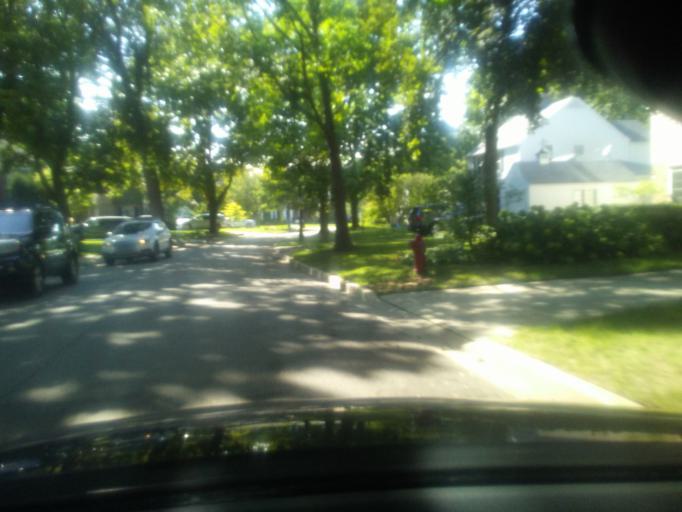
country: US
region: Illinois
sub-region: Cook County
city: Wilmette
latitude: 42.0546
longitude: -87.7120
